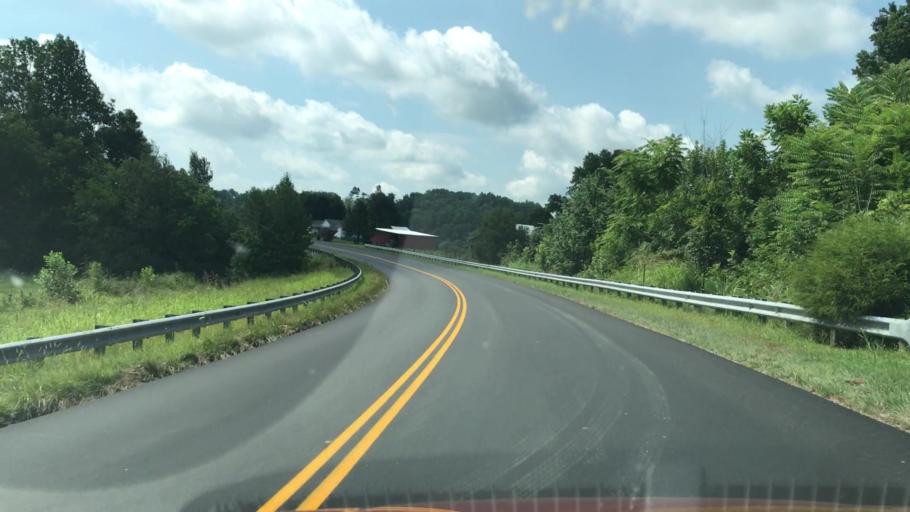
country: US
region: Kentucky
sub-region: Monroe County
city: Tompkinsville
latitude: 36.7677
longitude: -85.7993
